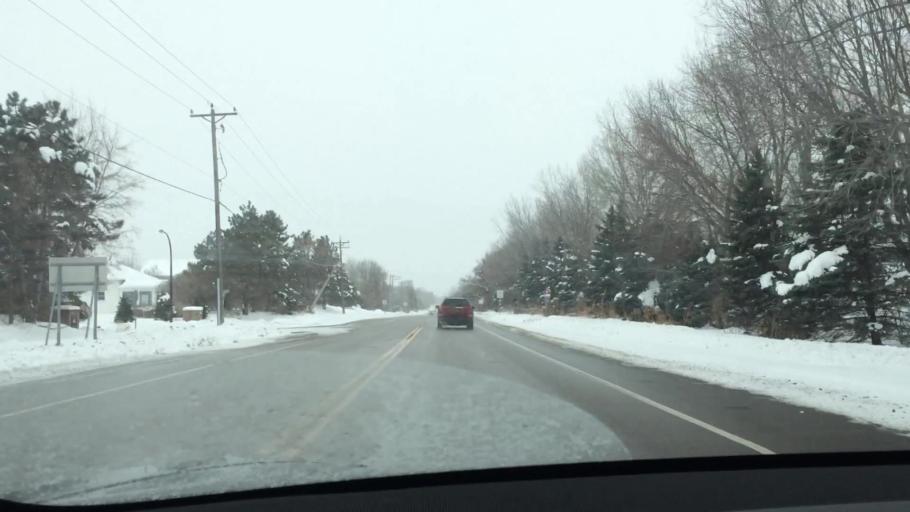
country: US
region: Minnesota
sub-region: Ramsey County
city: Shoreview
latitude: 45.1096
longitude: -93.1273
